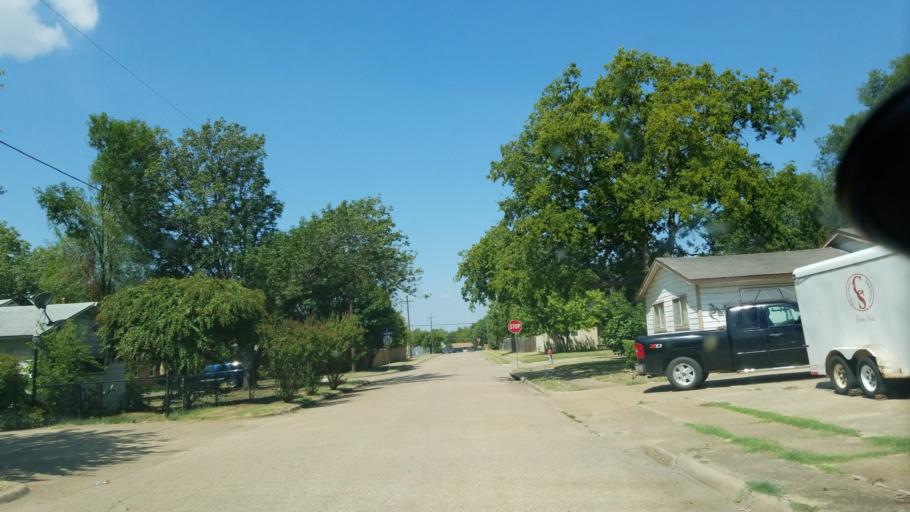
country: US
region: Texas
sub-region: Dallas County
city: Duncanville
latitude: 32.6581
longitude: -96.8973
